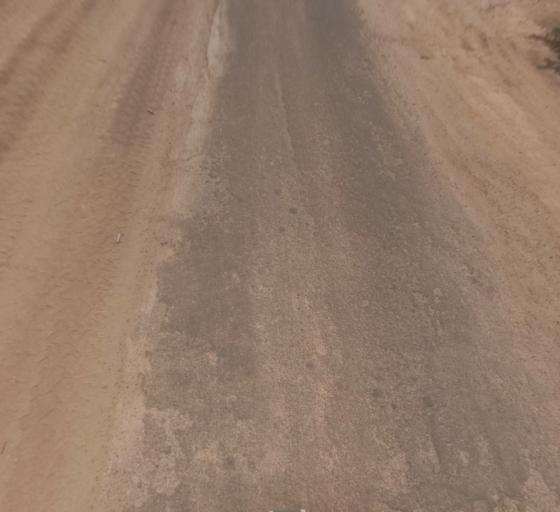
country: US
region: California
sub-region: Madera County
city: Fairmead
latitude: 37.1342
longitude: -120.1425
